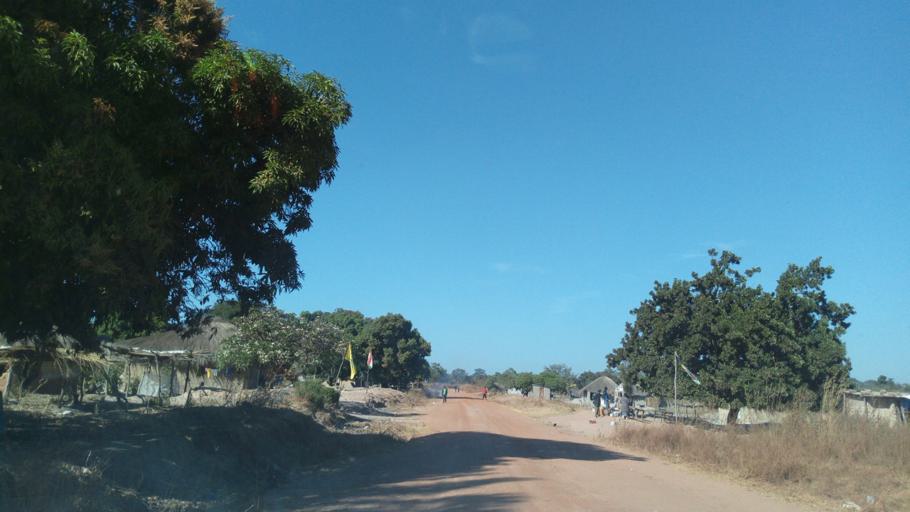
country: ZM
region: Luapula
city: Mwense
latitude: -10.6281
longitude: 28.4111
